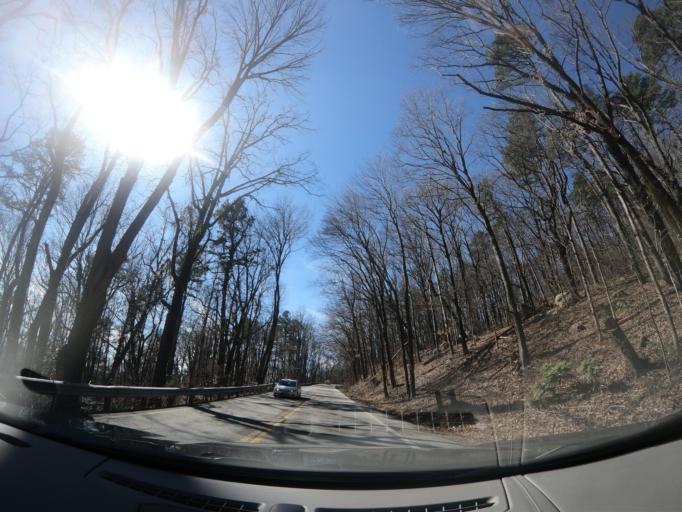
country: US
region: Tennessee
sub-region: Hamilton County
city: Lookout Mountain
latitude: 34.9970
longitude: -85.3364
